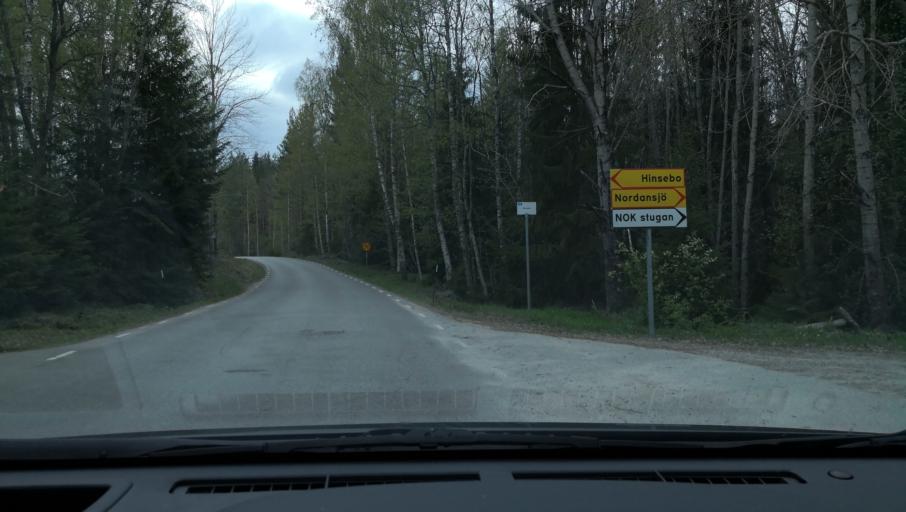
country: SE
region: Vaestmanland
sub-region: Norbergs Kommun
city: Norberg
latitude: 60.0905
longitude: 15.8961
